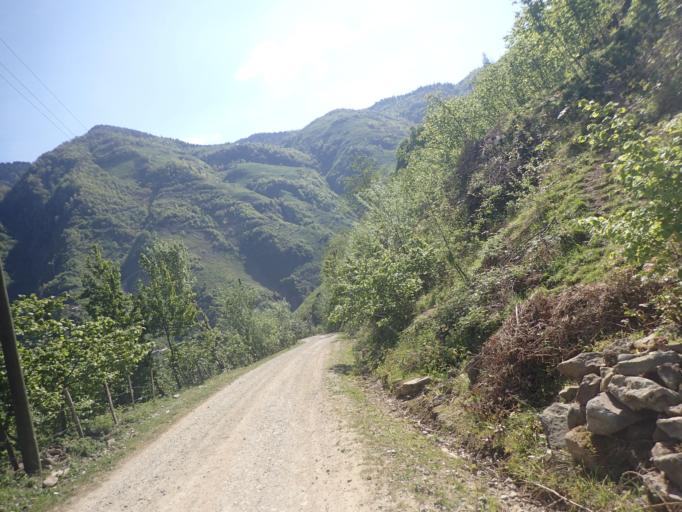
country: TR
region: Ordu
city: Topcam
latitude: 40.7097
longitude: 37.8731
